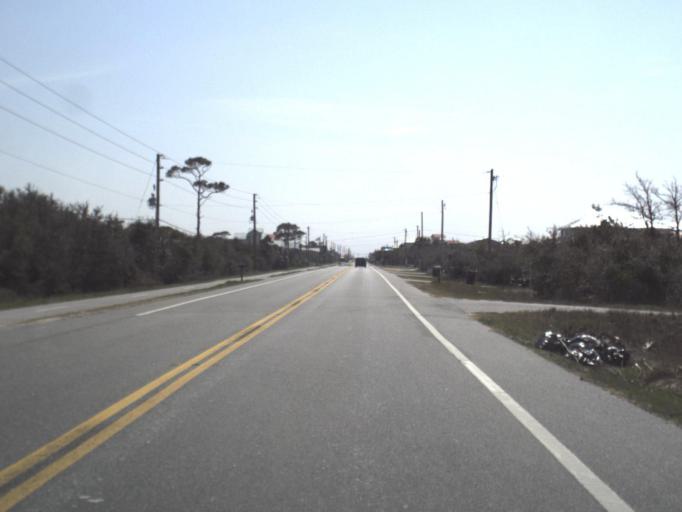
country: US
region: Florida
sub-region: Gulf County
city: Port Saint Joe
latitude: 29.6993
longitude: -85.3762
